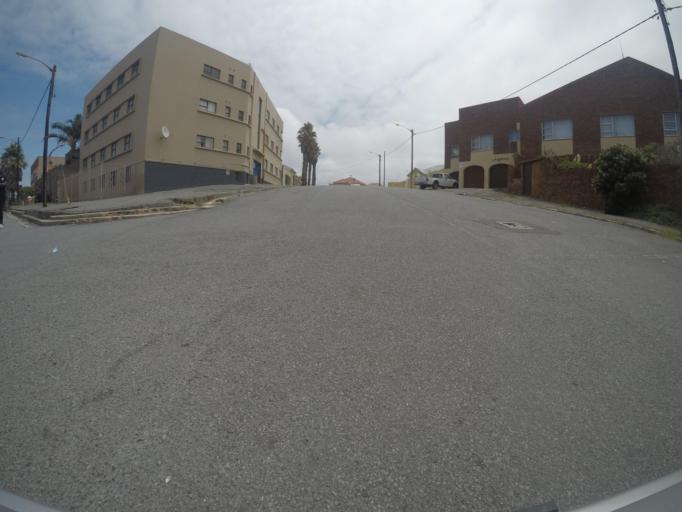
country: ZA
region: Eastern Cape
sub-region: Buffalo City Metropolitan Municipality
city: East London
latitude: -33.0164
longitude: 27.9179
